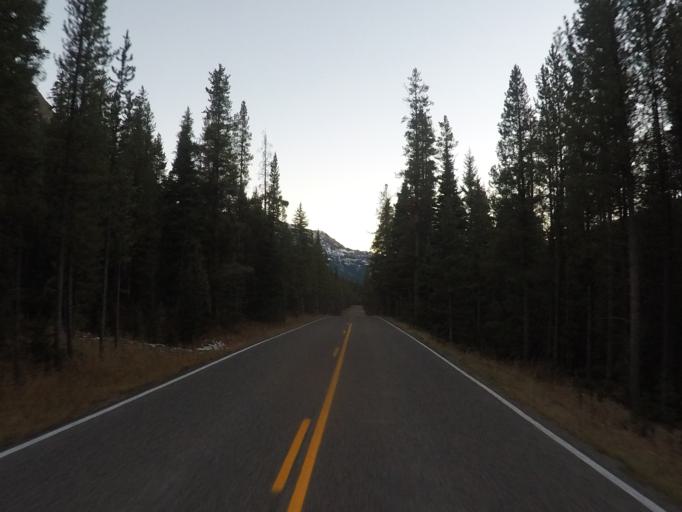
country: US
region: Montana
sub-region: Stillwater County
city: Absarokee
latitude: 44.9627
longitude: -110.0708
